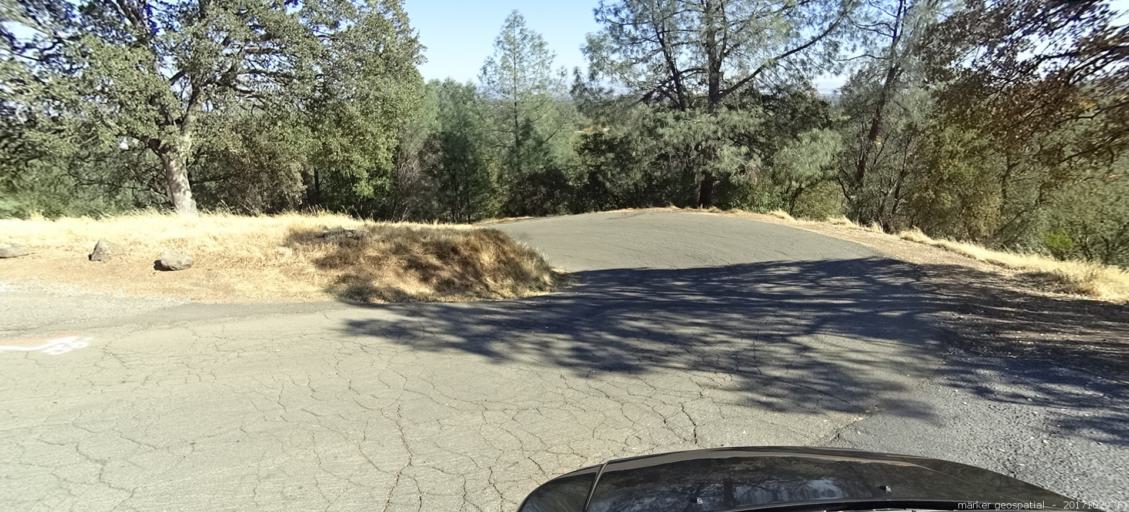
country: US
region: California
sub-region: Shasta County
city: Anderson
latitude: 40.4637
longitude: -122.3373
